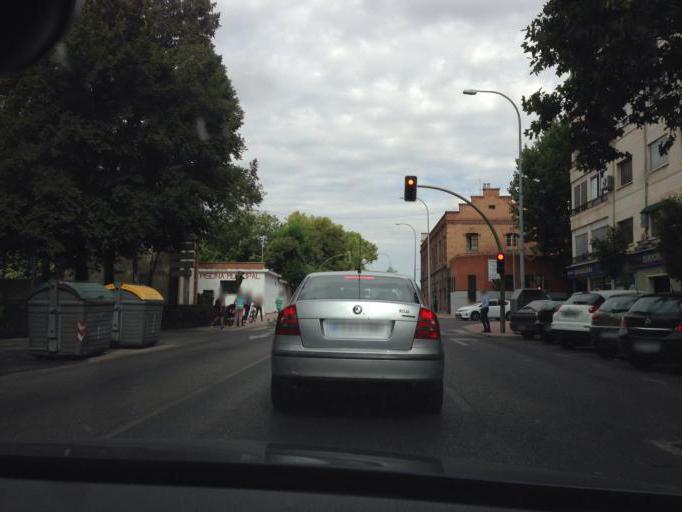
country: ES
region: Madrid
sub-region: Provincia de Madrid
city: Alcala de Henares
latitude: 40.4849
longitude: -3.3695
